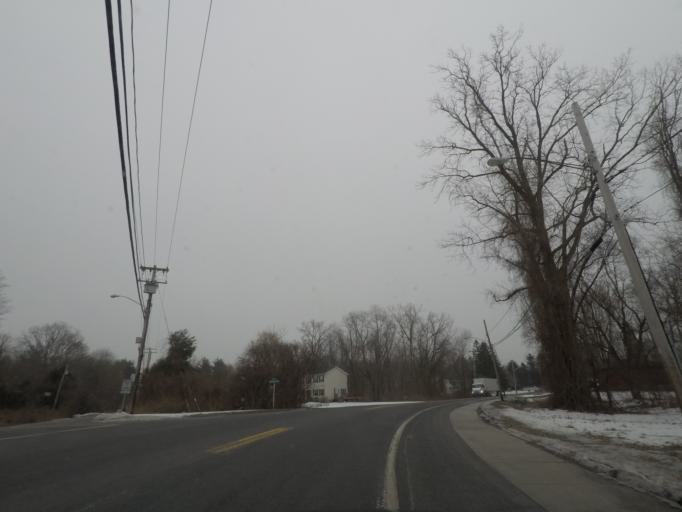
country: US
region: New York
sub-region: Rensselaer County
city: Castleton-on-Hudson
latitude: 42.5459
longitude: -73.8026
